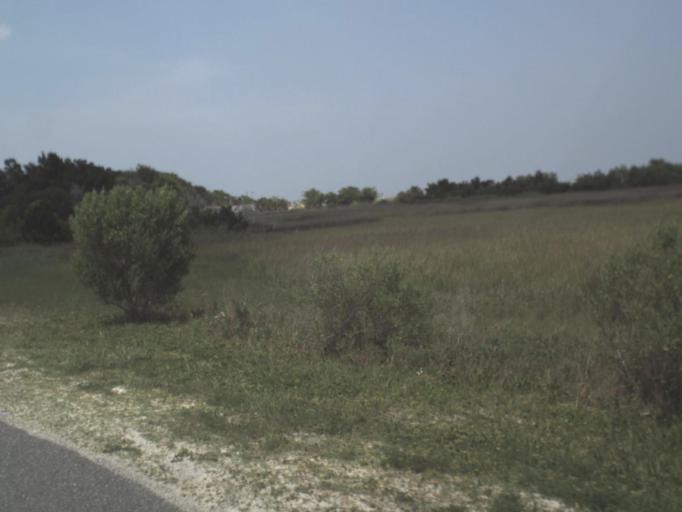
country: US
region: Florida
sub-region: Duval County
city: Atlantic Beach
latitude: 30.3815
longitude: -81.4384
